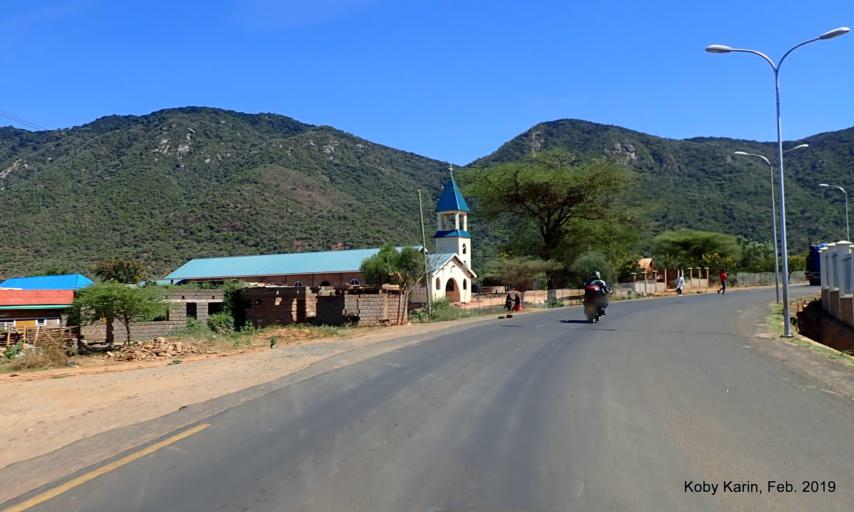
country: TZ
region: Arusha
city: Namanga
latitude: -2.5492
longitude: 36.7838
